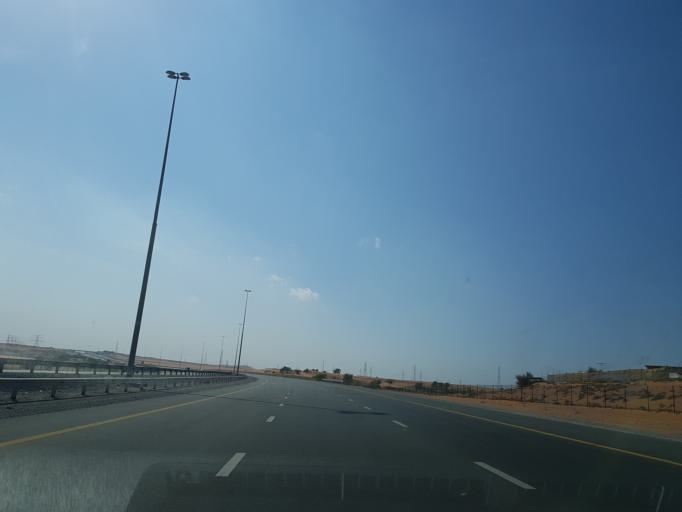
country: AE
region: Ra's al Khaymah
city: Ras al-Khaimah
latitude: 25.7060
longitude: 55.9405
